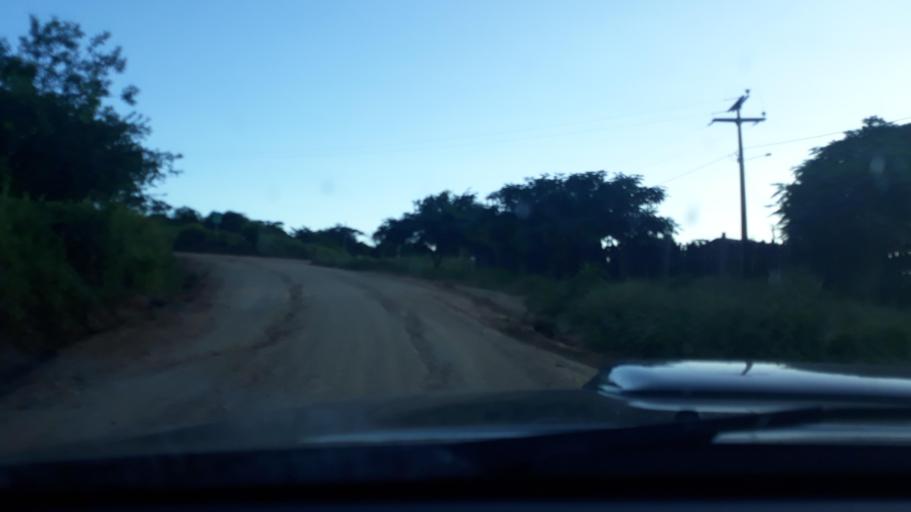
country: BR
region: Bahia
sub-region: Riacho De Santana
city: Riacho de Santana
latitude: -13.8348
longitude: -42.7310
